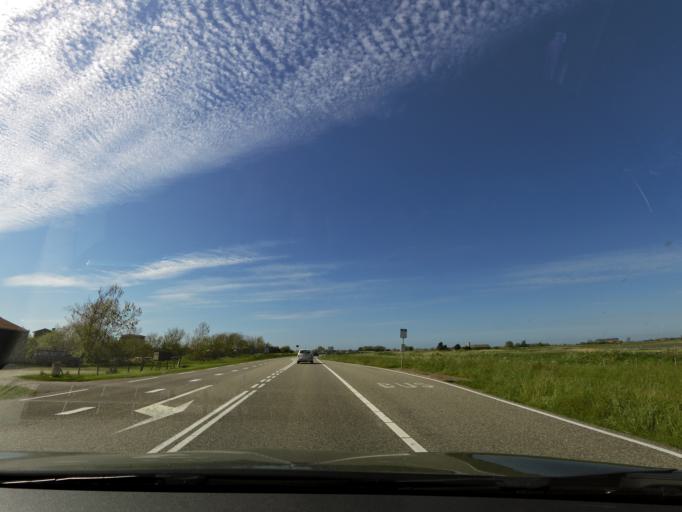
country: NL
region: Zeeland
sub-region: Schouwen-Duiveland
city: Scharendijke
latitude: 51.6746
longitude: 3.8676
